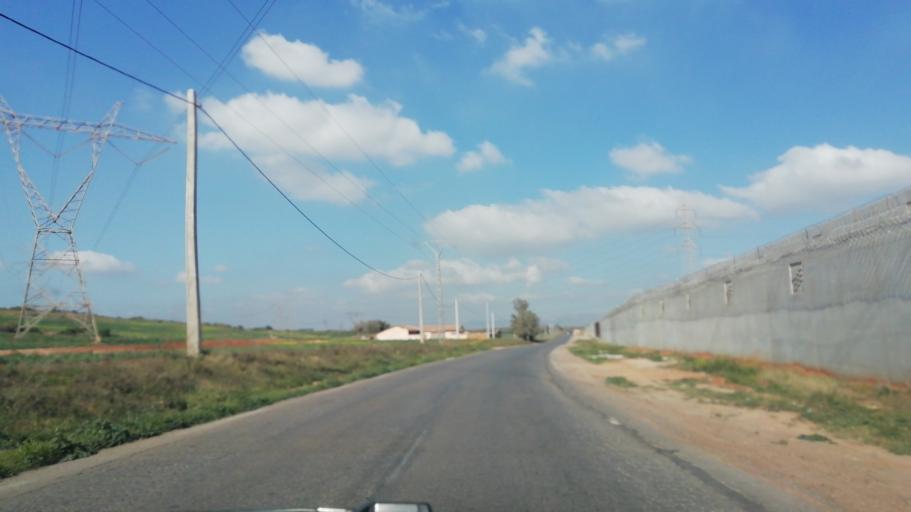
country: DZ
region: Oran
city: Ain el Bya
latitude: 35.7511
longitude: -0.2654
